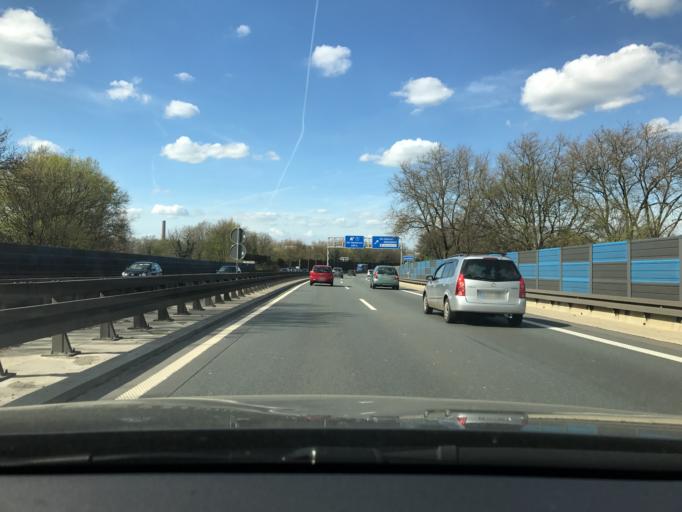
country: DE
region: North Rhine-Westphalia
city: Meiderich
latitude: 51.4619
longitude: 6.7702
